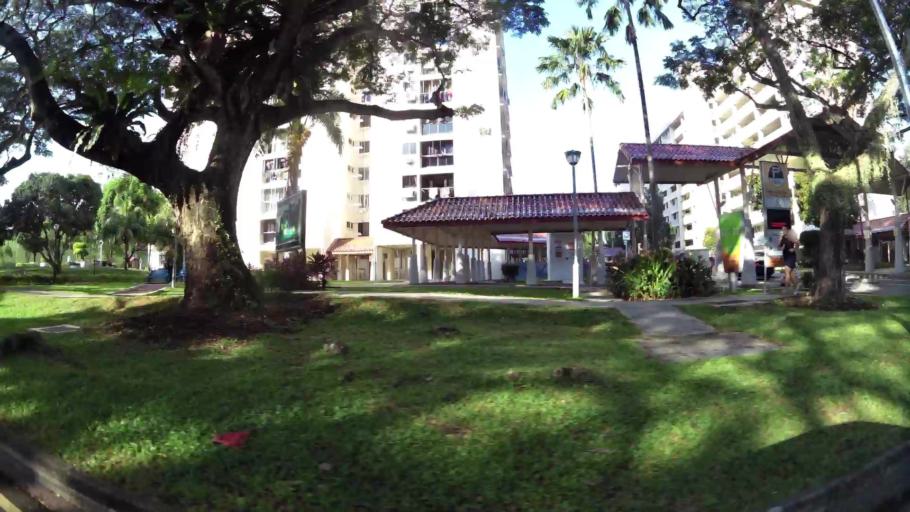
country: SG
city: Singapore
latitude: 1.3192
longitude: 103.9444
